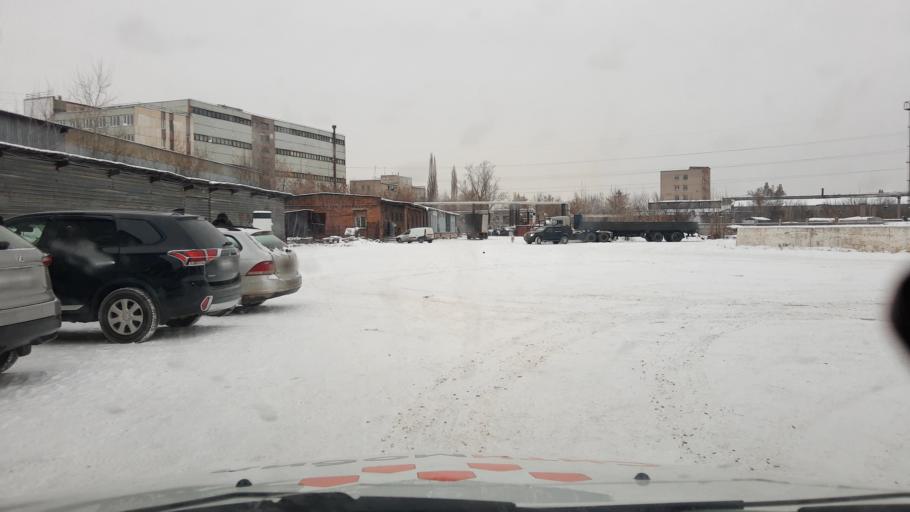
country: RU
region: Bashkortostan
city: Ufa
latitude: 54.7903
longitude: 56.0618
